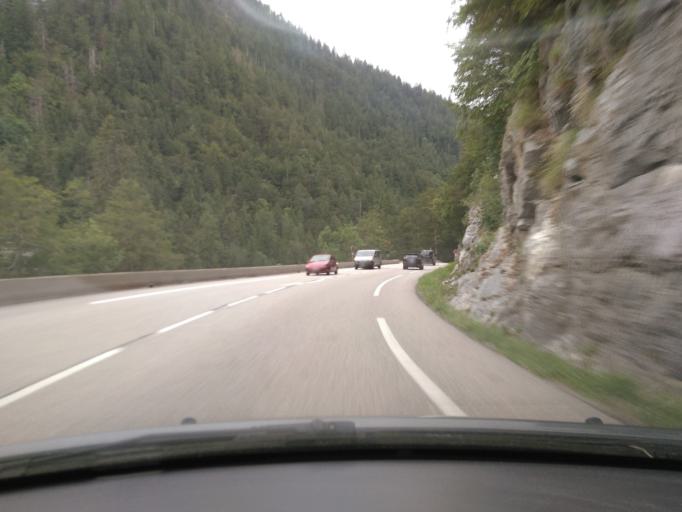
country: FR
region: Rhone-Alpes
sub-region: Departement de la Haute-Savoie
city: La Clusaz
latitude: 45.9070
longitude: 6.4204
